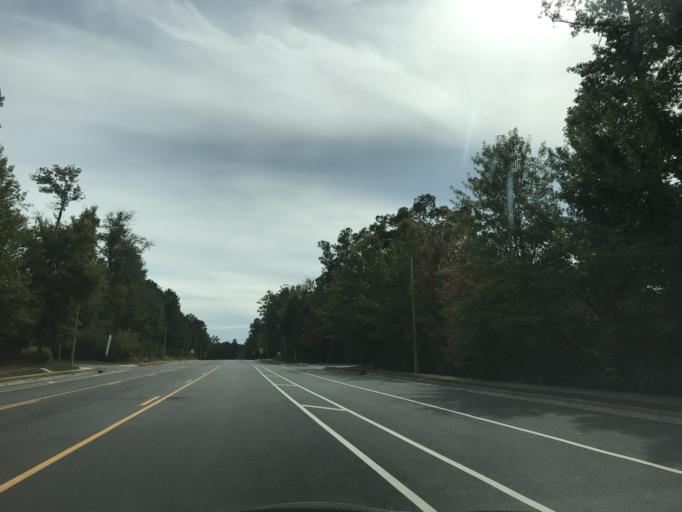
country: US
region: North Carolina
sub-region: Wake County
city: Wake Forest
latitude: 35.9527
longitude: -78.5457
